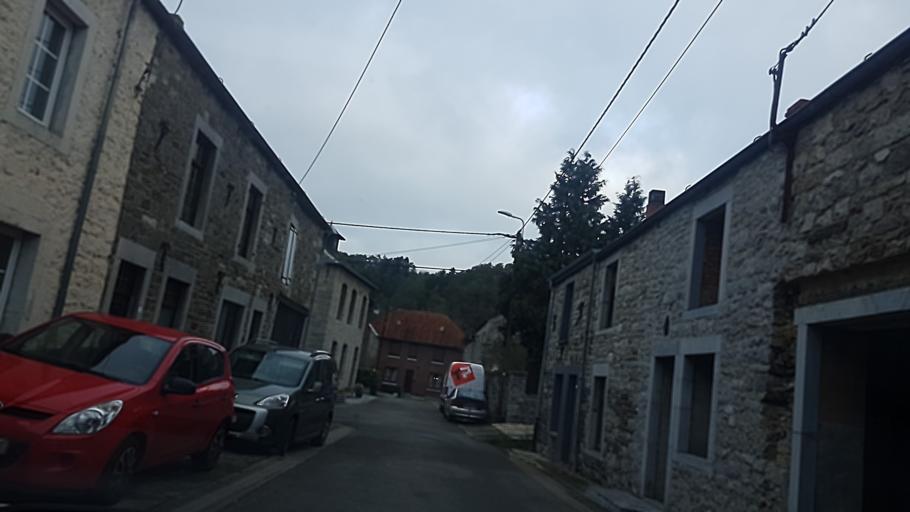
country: FR
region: Champagne-Ardenne
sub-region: Departement des Ardennes
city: Vireux-Molhain
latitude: 50.0743
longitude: 4.6087
